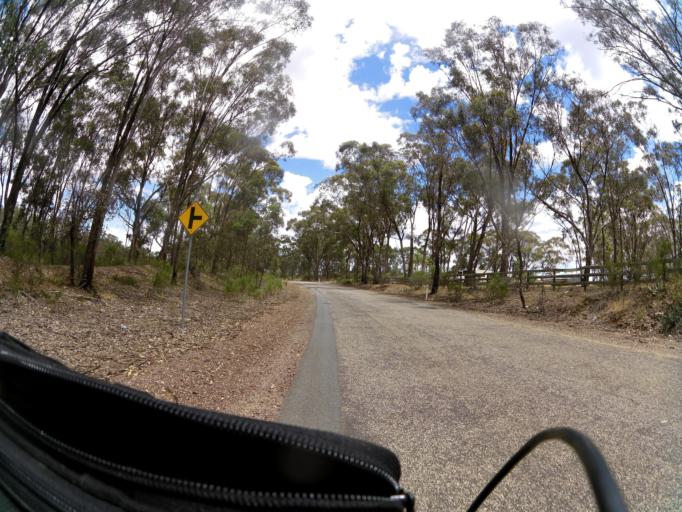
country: AU
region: Victoria
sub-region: Greater Shepparton
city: Shepparton
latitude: -36.6922
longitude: 145.1752
